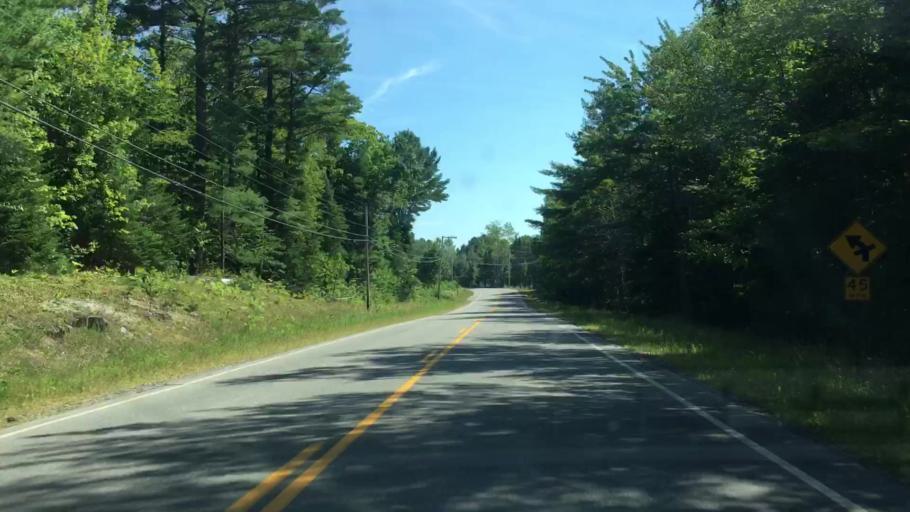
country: US
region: Maine
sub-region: Piscataquis County
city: Milo
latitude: 45.1905
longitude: -68.8974
